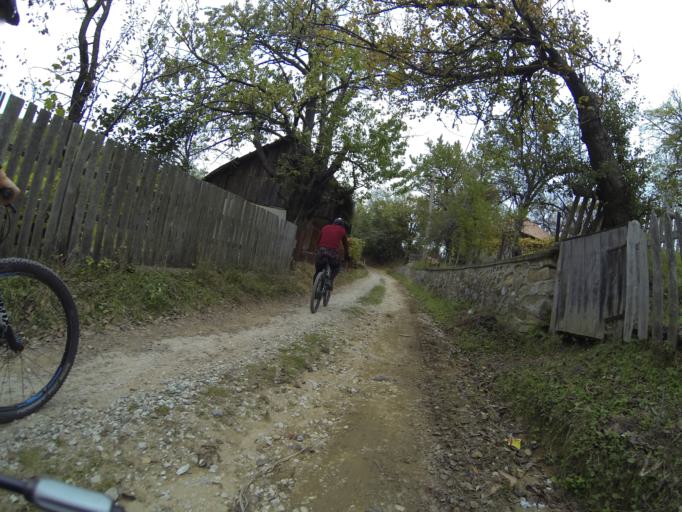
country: RO
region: Gorj
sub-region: Comuna Tismana
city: Sohodol
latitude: 45.0628
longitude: 22.8720
